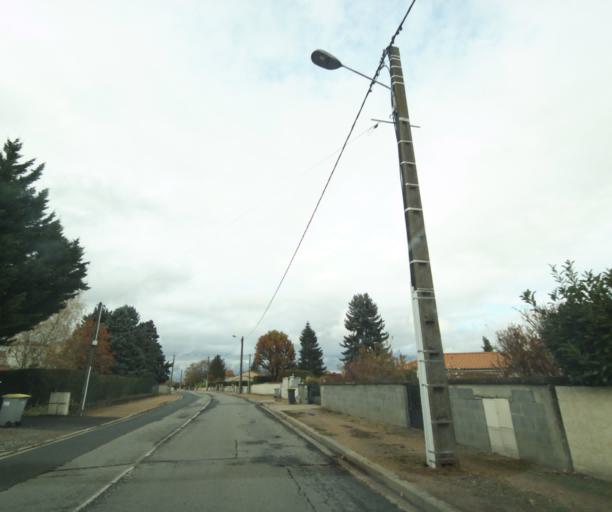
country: FR
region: Auvergne
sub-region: Departement du Puy-de-Dome
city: Pont-du-Chateau
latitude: 45.8079
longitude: 3.2431
